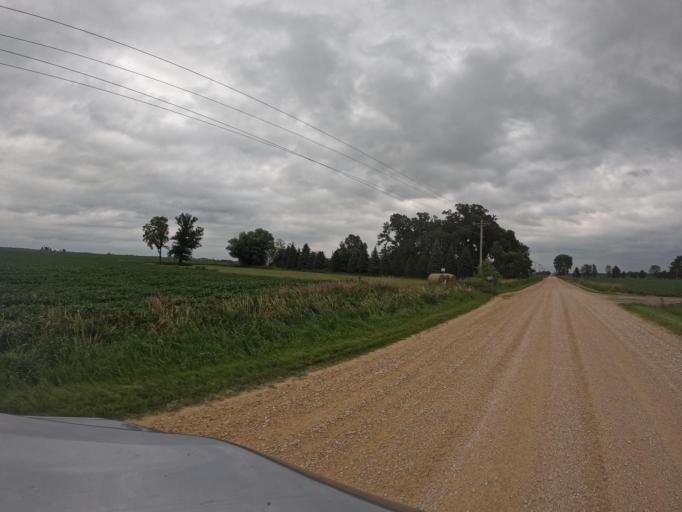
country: US
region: Iowa
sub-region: Clinton County
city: De Witt
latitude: 41.7864
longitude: -90.4506
